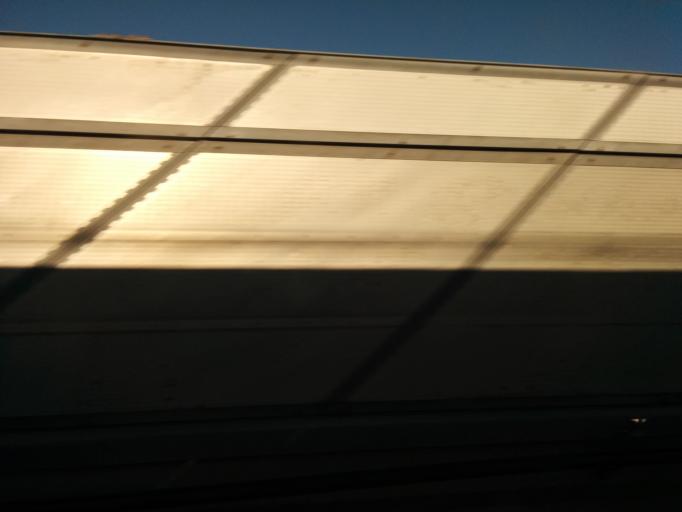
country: JP
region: Kanagawa
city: Isehara
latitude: 35.3601
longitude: 139.3264
